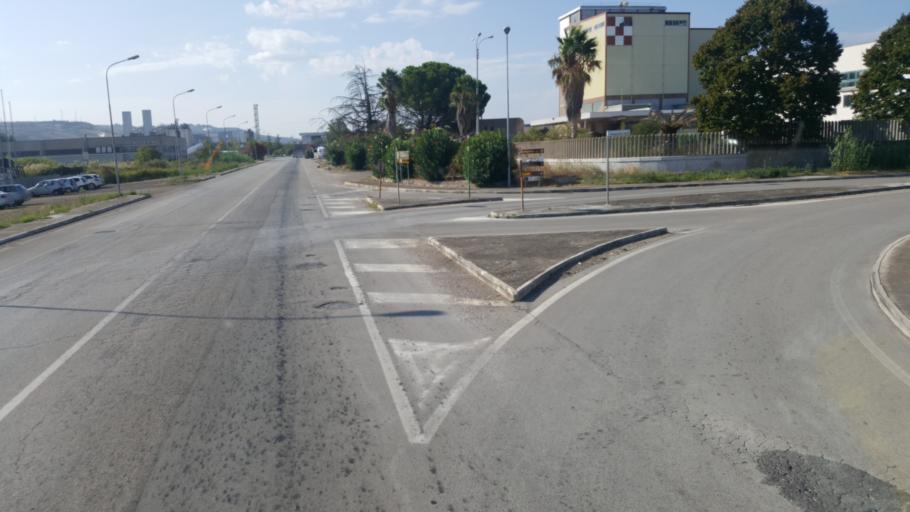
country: IT
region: Molise
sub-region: Provincia di Campobasso
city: Portocannone
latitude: 41.9449
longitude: 14.9995
